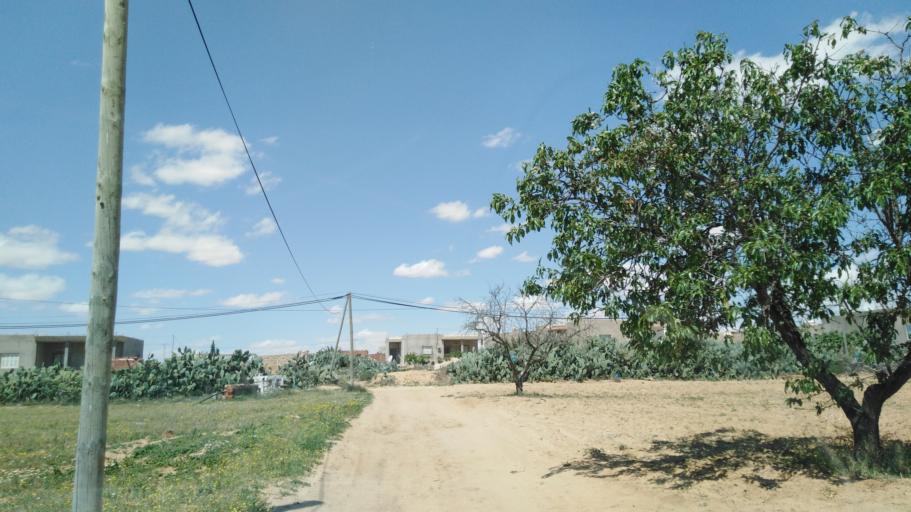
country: TN
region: Safaqis
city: Sfax
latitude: 34.7481
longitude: 10.5388
